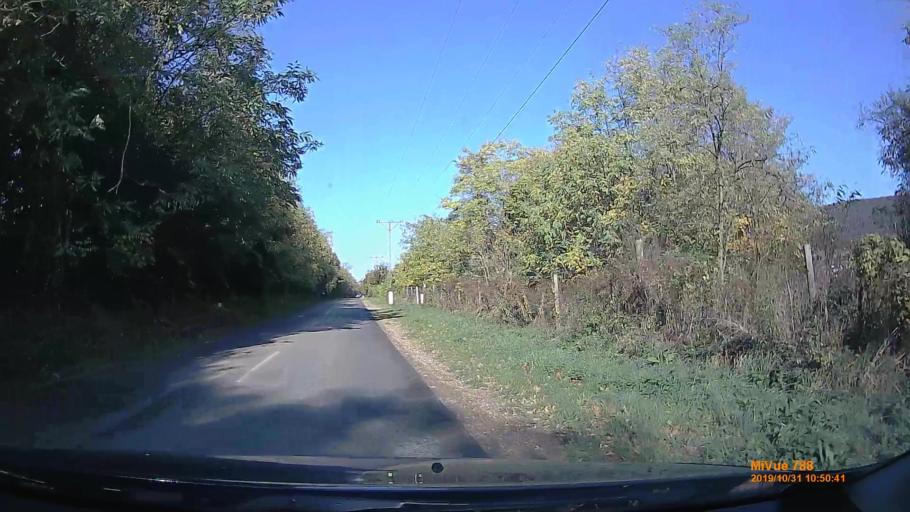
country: HU
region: Pest
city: Pilisborosjeno
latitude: 47.5988
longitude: 18.9973
